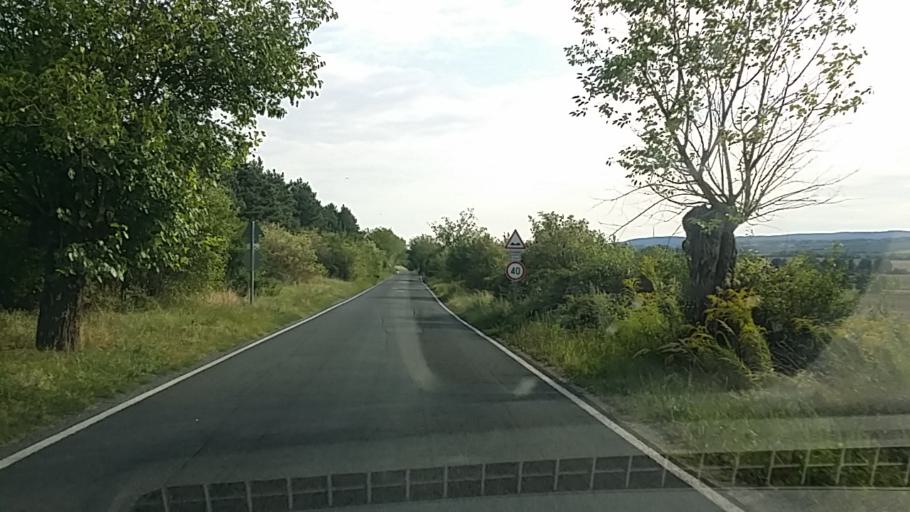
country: HU
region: Gyor-Moson-Sopron
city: Fertorakos
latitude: 47.7386
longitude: 16.6208
